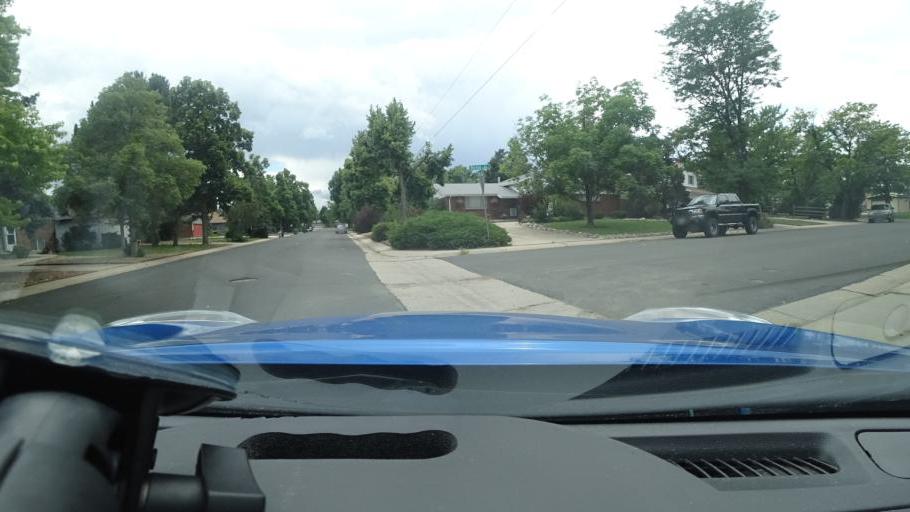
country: US
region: Colorado
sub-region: Adams County
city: Aurora
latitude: 39.7205
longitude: -104.8292
